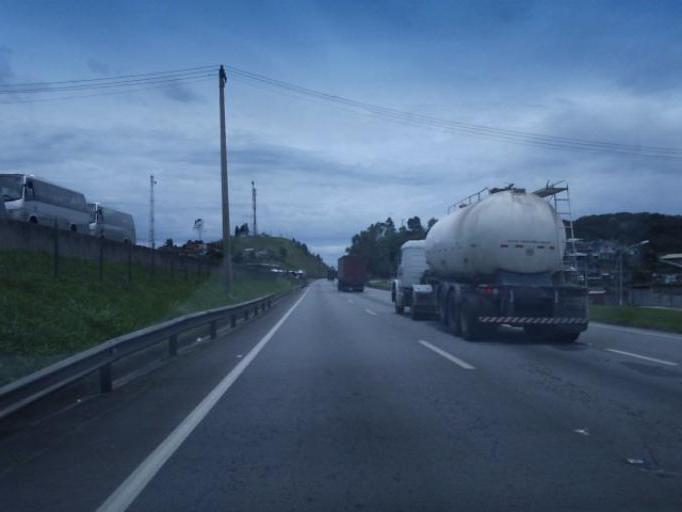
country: BR
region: Sao Paulo
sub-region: Juquitiba
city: Juquitiba
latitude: -23.9807
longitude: -47.1455
